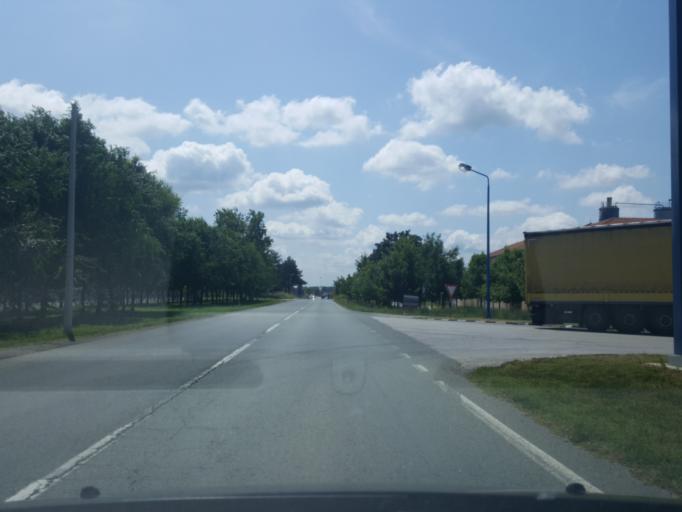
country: RS
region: Autonomna Pokrajina Vojvodina
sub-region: Sremski Okrug
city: Sremska Mitrovica
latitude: 44.9751
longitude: 19.6379
